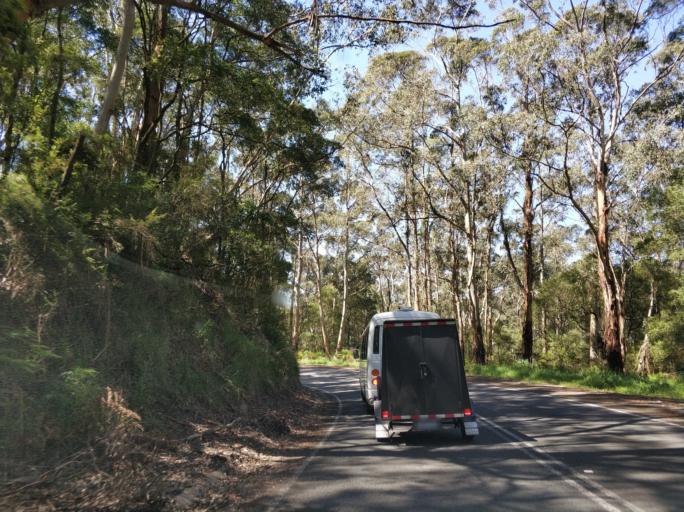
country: AU
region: Victoria
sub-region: Colac-Otway
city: Apollo Bay
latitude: -38.7368
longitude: 143.2509
